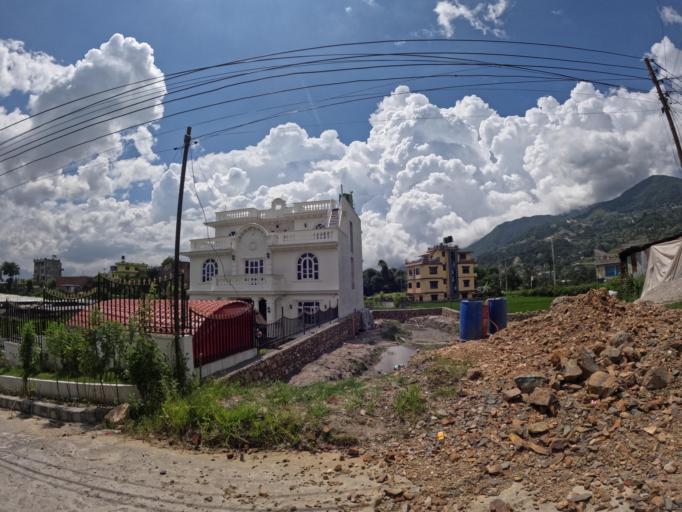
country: NP
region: Central Region
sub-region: Bagmati Zone
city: Kathmandu
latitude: 27.7846
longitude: 85.3275
